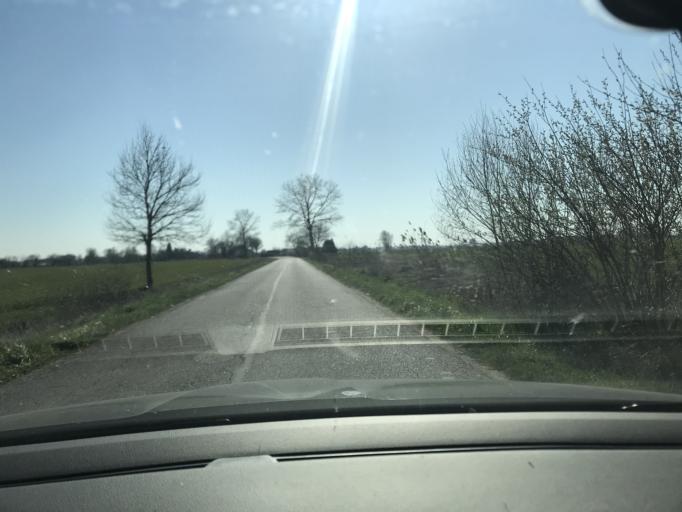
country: PL
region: Pomeranian Voivodeship
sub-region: Powiat nowodworski
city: Sztutowo
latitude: 54.3087
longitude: 19.1546
